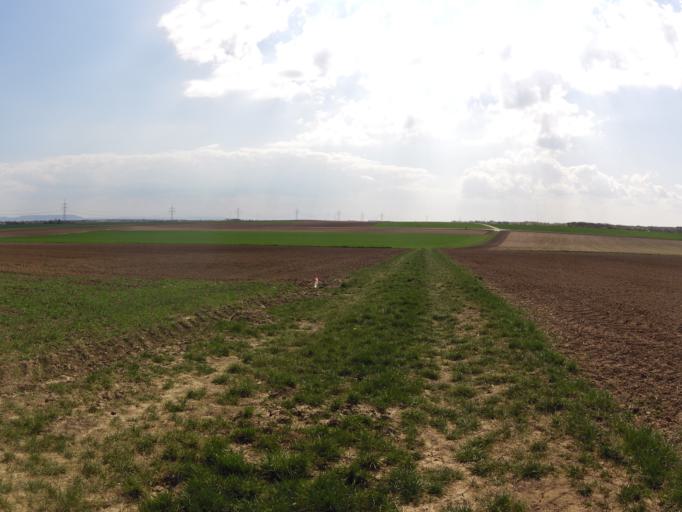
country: DE
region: Bavaria
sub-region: Regierungsbezirk Unterfranken
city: Oberpleichfeld
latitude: 49.8441
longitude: 10.0763
